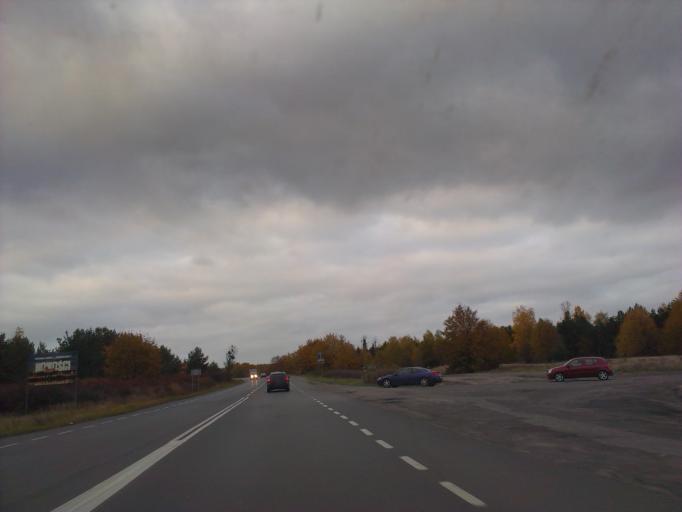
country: PL
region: Kujawsko-Pomorskie
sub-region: Torun
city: Torun
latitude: 53.0433
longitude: 18.6154
